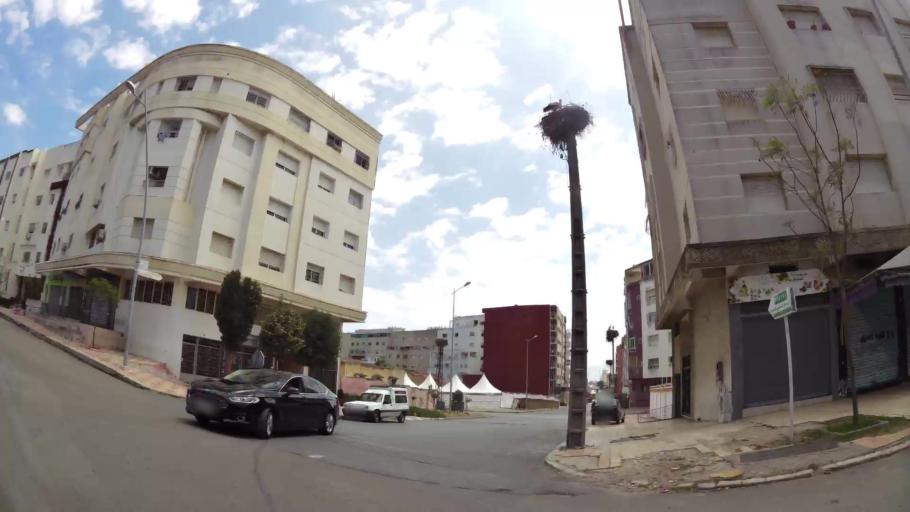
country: MA
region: Gharb-Chrarda-Beni Hssen
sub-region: Kenitra Province
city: Kenitra
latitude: 34.2661
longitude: -6.5928
